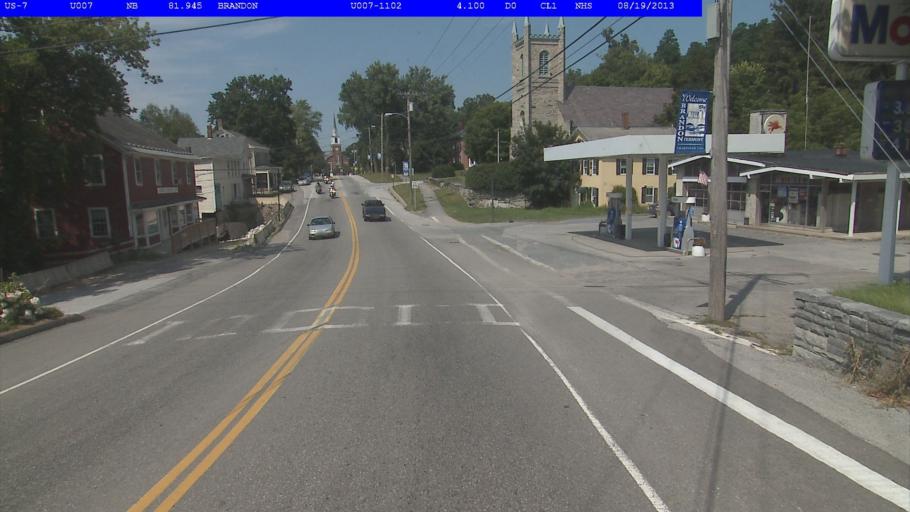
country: US
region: Vermont
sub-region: Rutland County
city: Brandon
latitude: 43.7997
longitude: -73.0895
